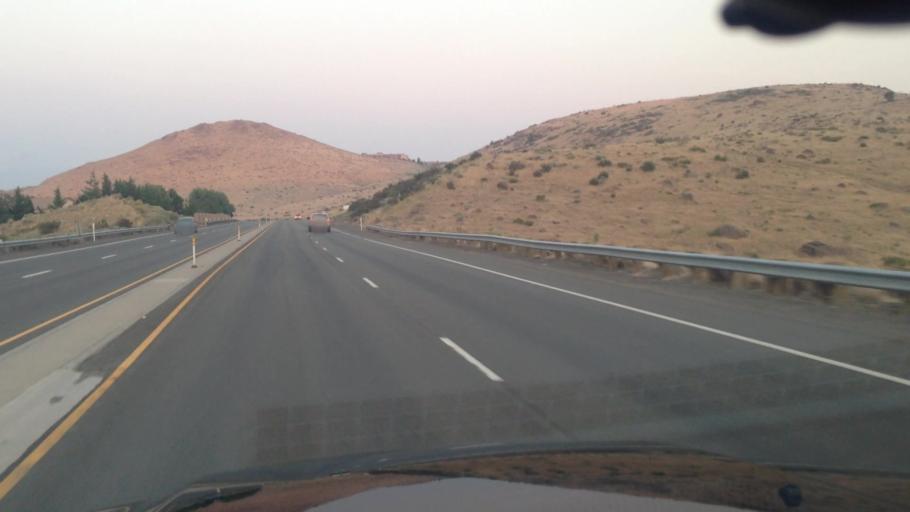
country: US
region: Nevada
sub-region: Washoe County
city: Reno
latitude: 39.4758
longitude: -119.8422
